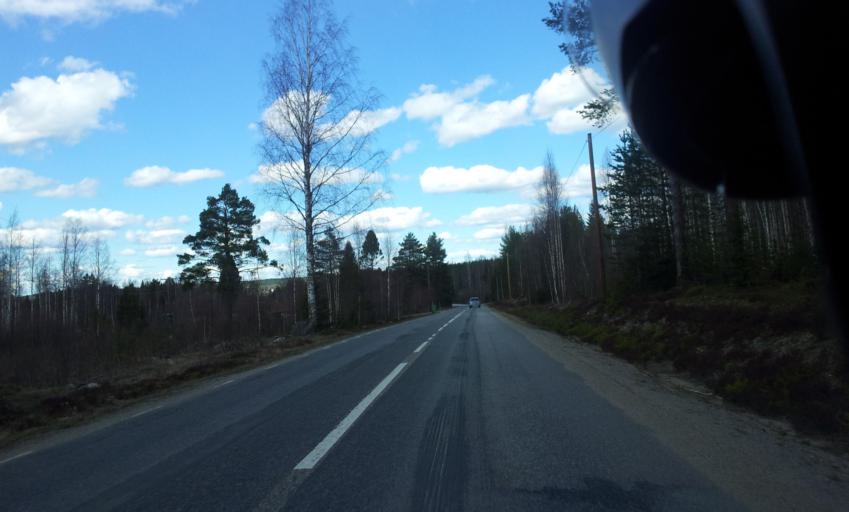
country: SE
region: Gaevleborg
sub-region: Ovanakers Kommun
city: Edsbyn
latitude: 61.2959
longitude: 15.8907
